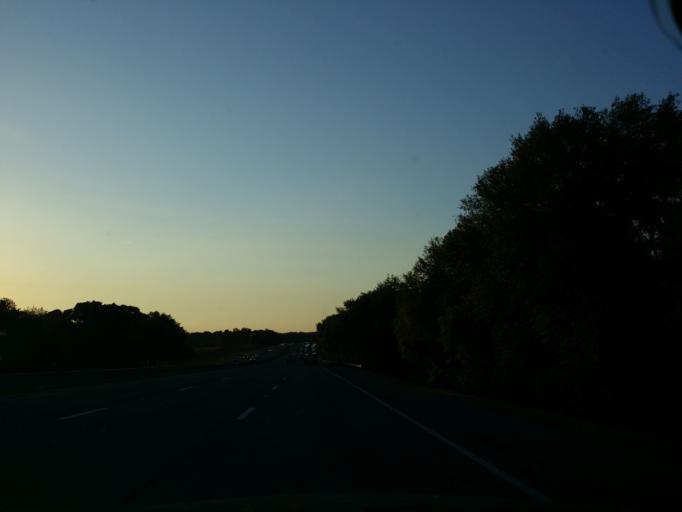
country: US
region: Florida
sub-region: Columbia County
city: Five Points
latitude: 30.2310
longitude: -82.7262
